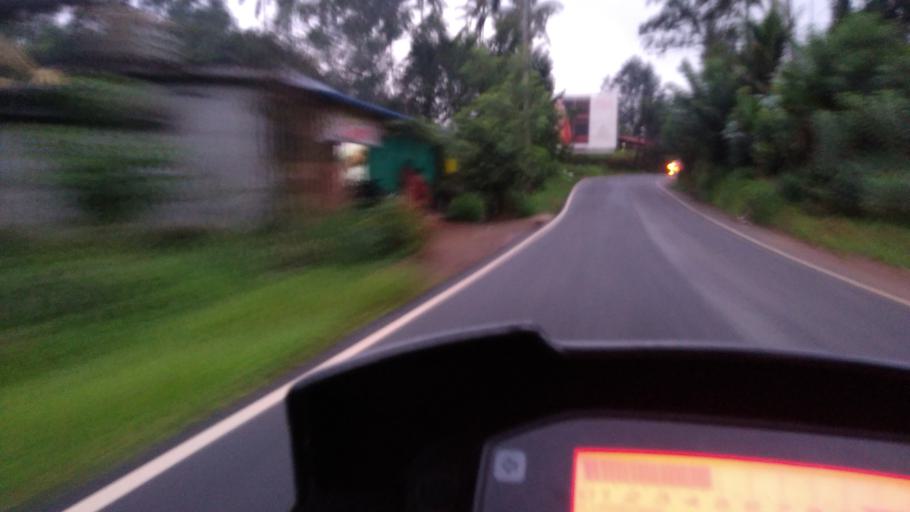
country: IN
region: Kerala
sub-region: Idukki
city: Munnar
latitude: 9.9568
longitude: 77.0848
